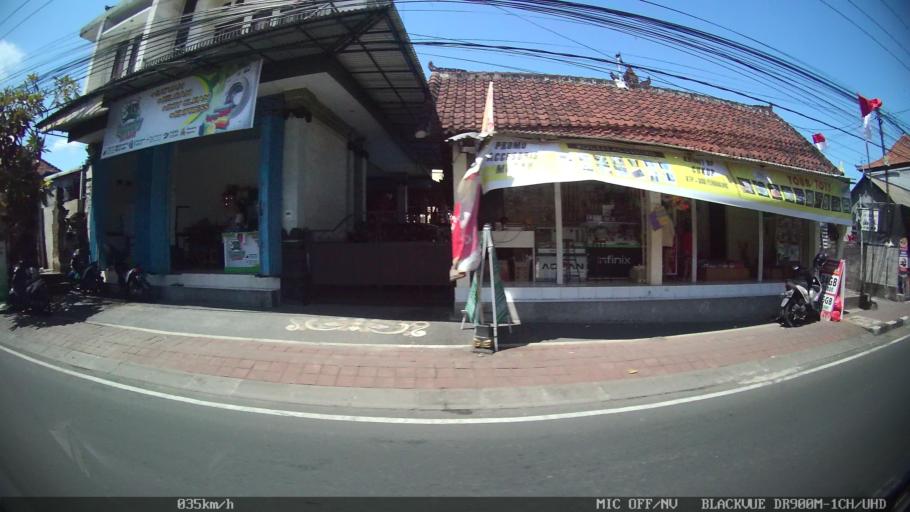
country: ID
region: Bali
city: Banjar Gunungpande
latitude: -8.6490
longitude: 115.1726
